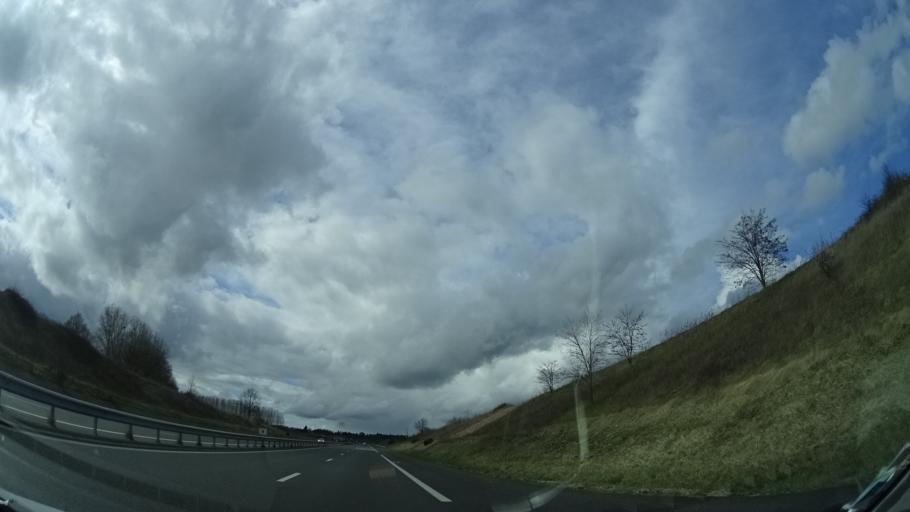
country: FR
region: Rhone-Alpes
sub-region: Departement de la Loire
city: La Pacaudiere
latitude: 46.1847
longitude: 3.8712
